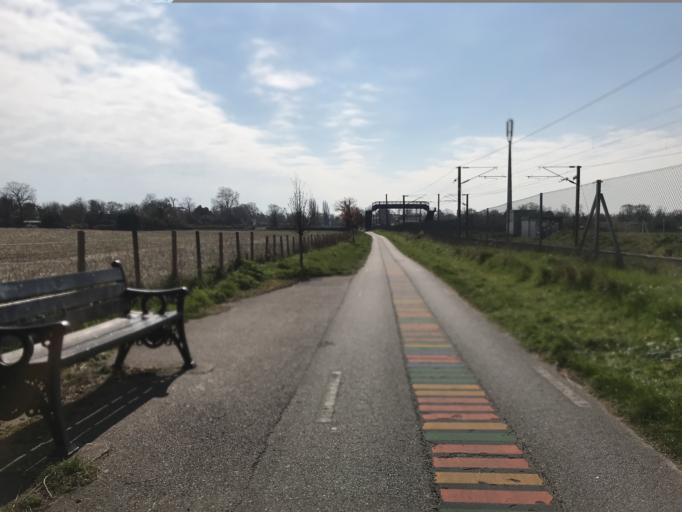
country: GB
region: England
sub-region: Cambridgeshire
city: Cambridge
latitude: 52.1589
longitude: 0.1344
